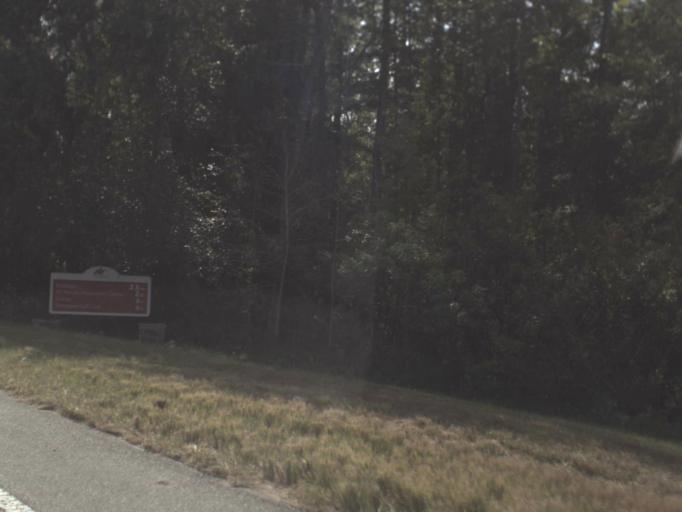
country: US
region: Florida
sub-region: Osceola County
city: Poinciana
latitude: 28.1988
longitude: -81.4738
